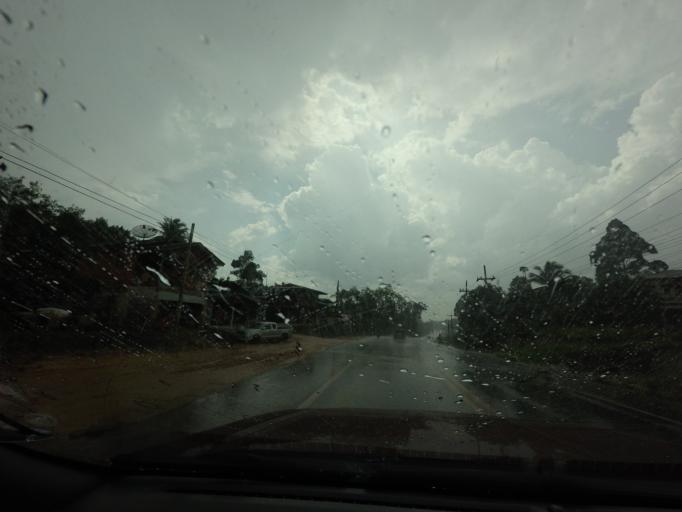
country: TH
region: Yala
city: Krong Pi Nang
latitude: 6.3870
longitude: 101.2916
